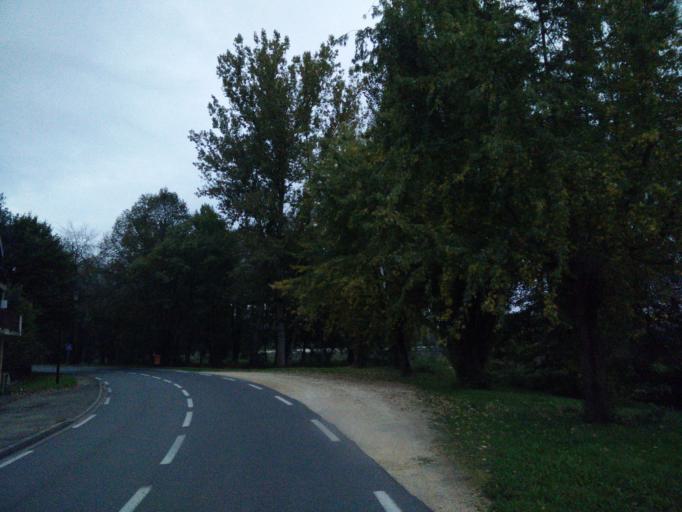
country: FR
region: Aquitaine
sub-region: Departement de la Dordogne
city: Carsac-Aillac
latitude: 44.8064
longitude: 1.2971
